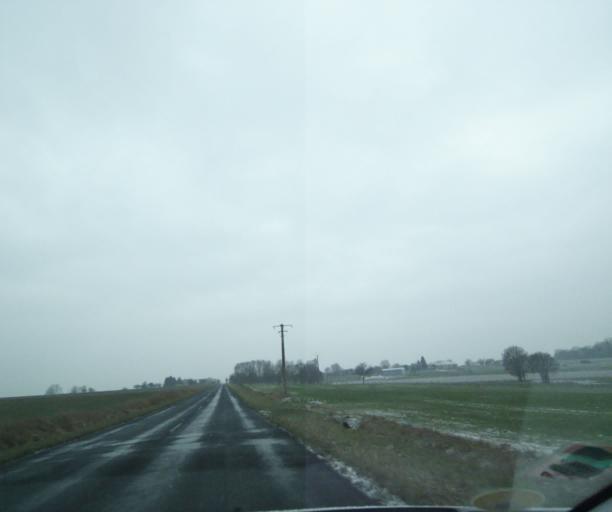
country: FR
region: Champagne-Ardenne
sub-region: Departement de la Haute-Marne
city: Wassy
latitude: 48.4652
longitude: 5.0292
